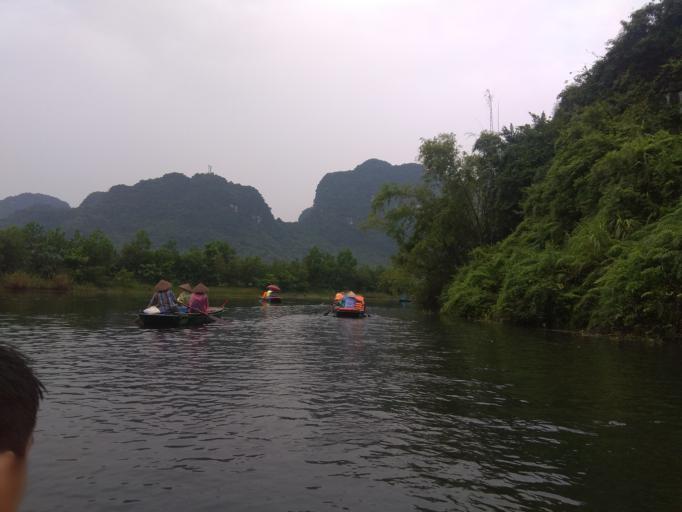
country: VN
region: Ninh Binh
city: Thi Tran Thien Ton
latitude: 20.2625
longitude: 105.9100
